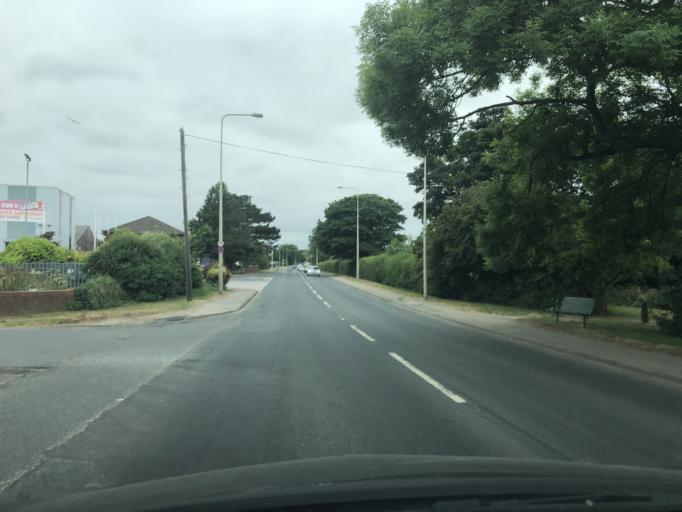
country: GB
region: England
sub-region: North Yorkshire
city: Scarborough
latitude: 54.2379
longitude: -0.4005
